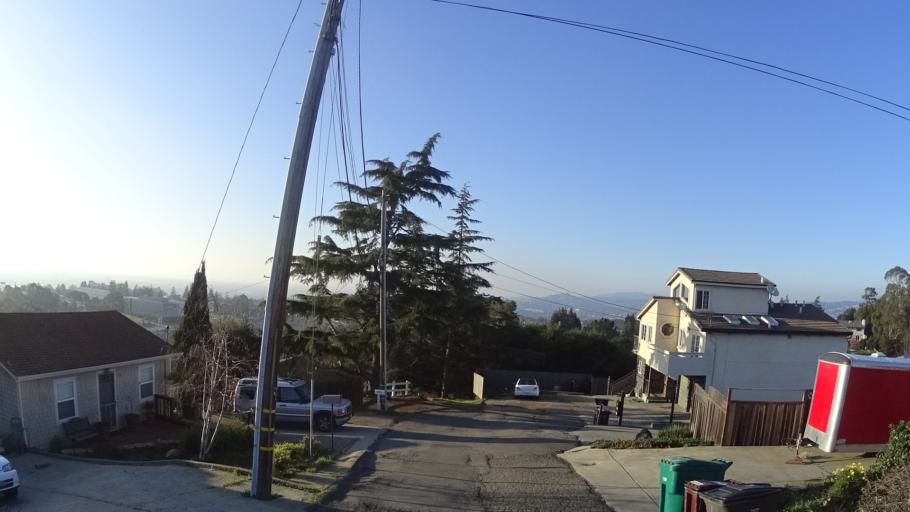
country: US
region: California
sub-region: Alameda County
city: Fairview
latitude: 37.6570
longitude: -122.0470
